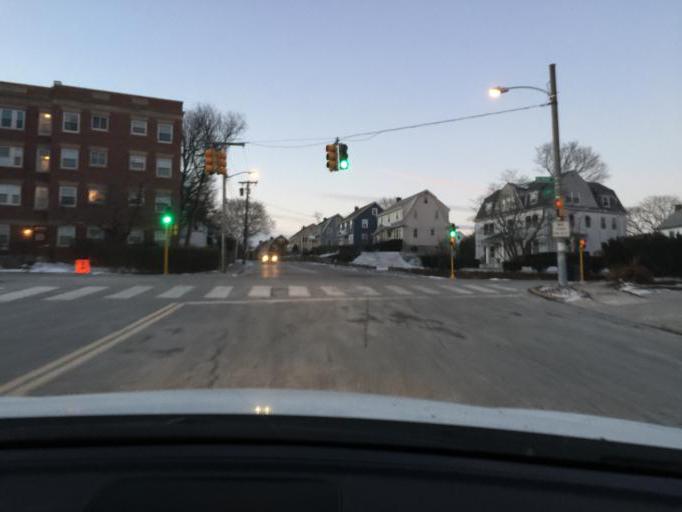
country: US
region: Massachusetts
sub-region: Middlesex County
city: Watertown
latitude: 42.3797
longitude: -71.1752
